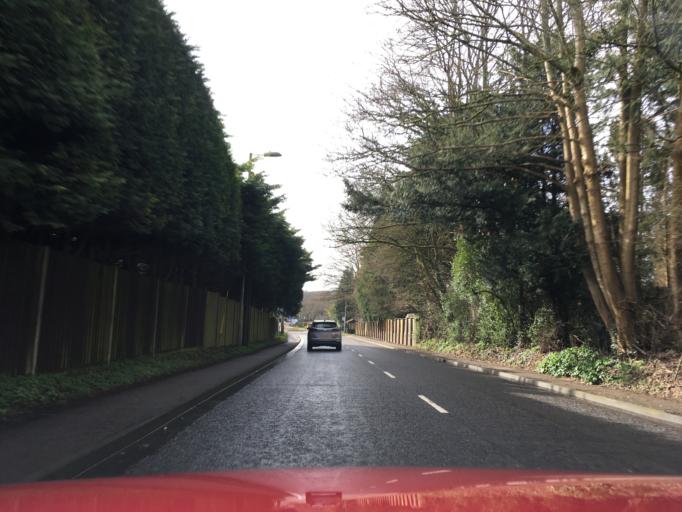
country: GB
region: England
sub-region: Hampshire
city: Compton
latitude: 51.0111
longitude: -1.3416
